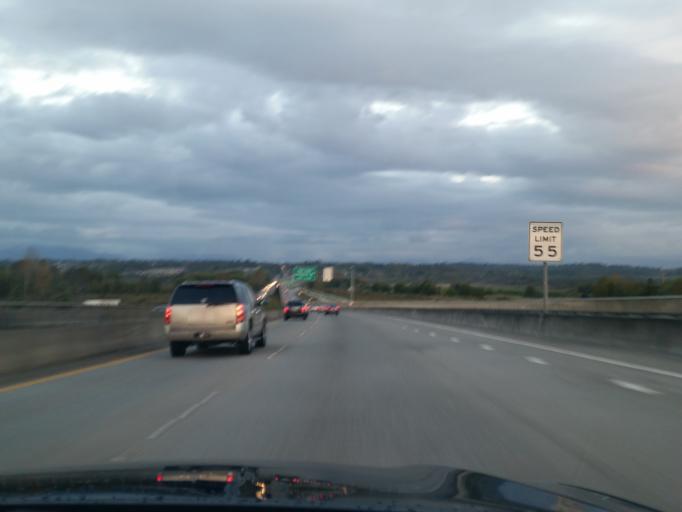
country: US
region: Washington
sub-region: Snohomish County
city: Everett
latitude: 47.9783
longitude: -122.1785
